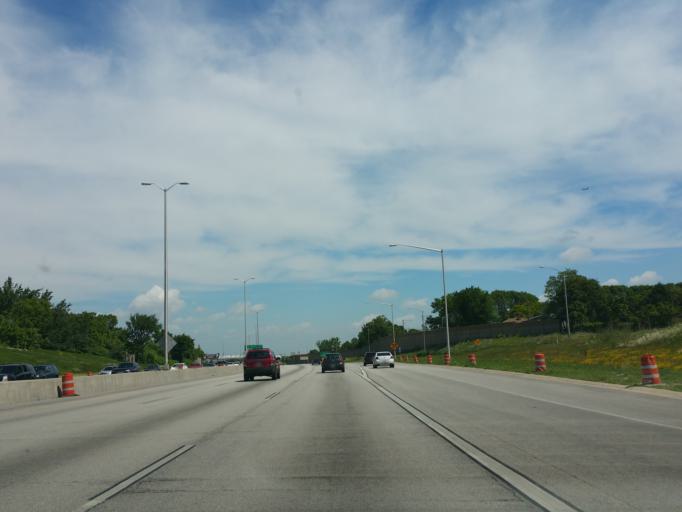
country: US
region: Wisconsin
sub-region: Milwaukee County
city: Saint Francis
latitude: 42.9741
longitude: -87.9154
